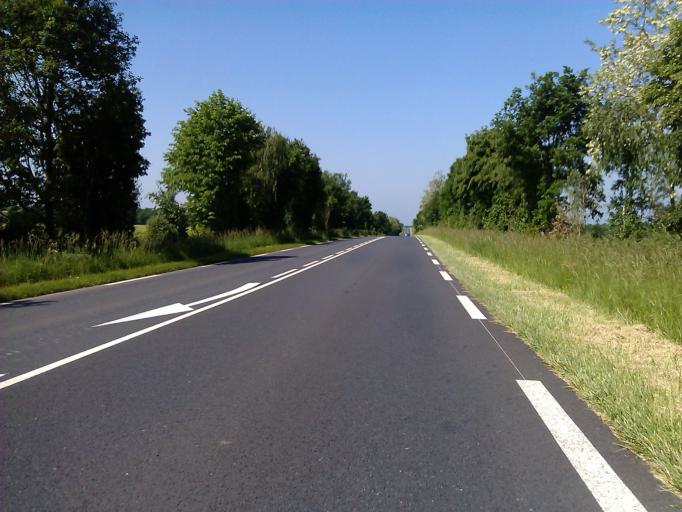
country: FR
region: Centre
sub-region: Departement de l'Indre
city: Le Pechereau
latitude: 46.6018
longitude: 1.6173
